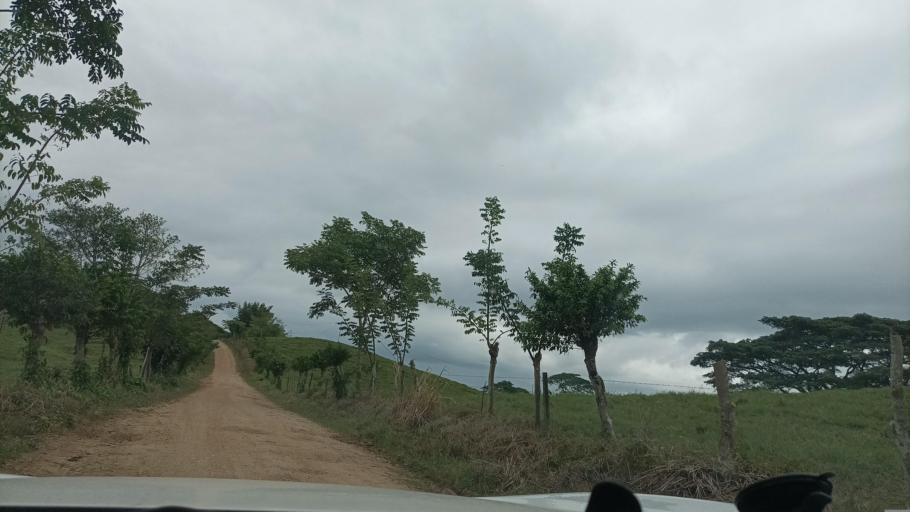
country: MX
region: Veracruz
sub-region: Uxpanapa
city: Poblado Cinco
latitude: 17.4957
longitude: -94.5660
